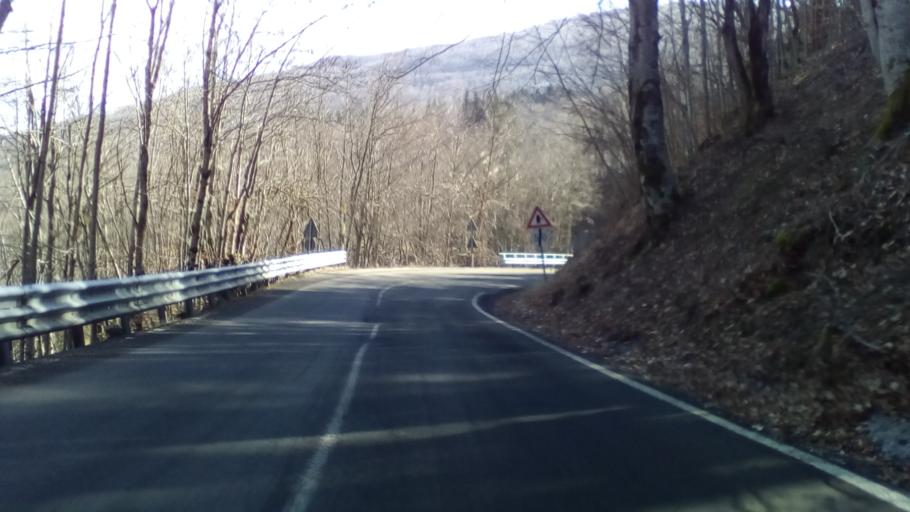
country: IT
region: Emilia-Romagna
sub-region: Provincia di Modena
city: Pievepelago
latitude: 44.1889
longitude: 10.5708
